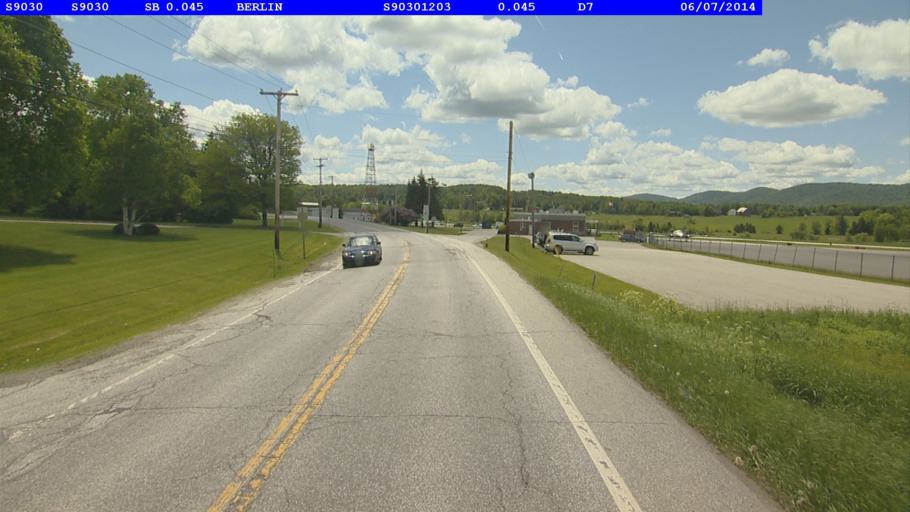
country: US
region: Vermont
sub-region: Washington County
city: Montpelier
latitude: 44.2040
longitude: -72.5622
